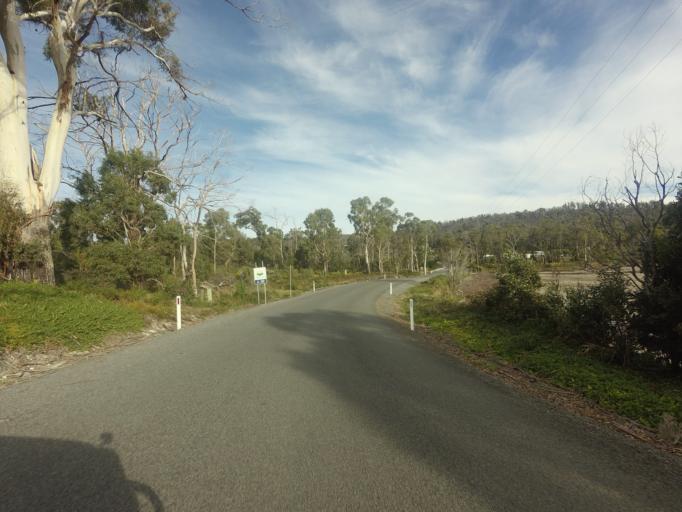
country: AU
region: Tasmania
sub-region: Sorell
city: Sorell
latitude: -42.9569
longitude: 147.8538
